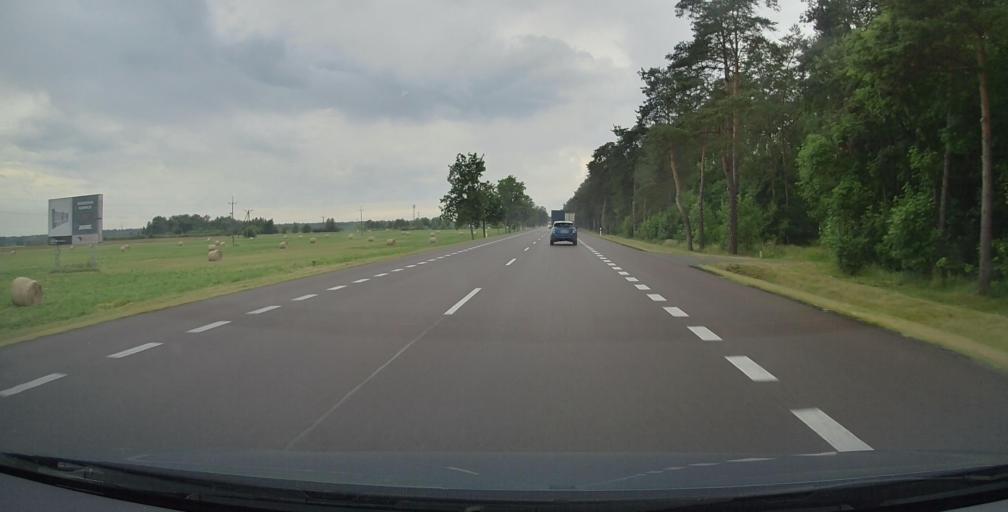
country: PL
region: Lublin Voivodeship
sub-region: Powiat bialski
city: Lesna Podlaska
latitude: 52.0381
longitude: 22.9595
